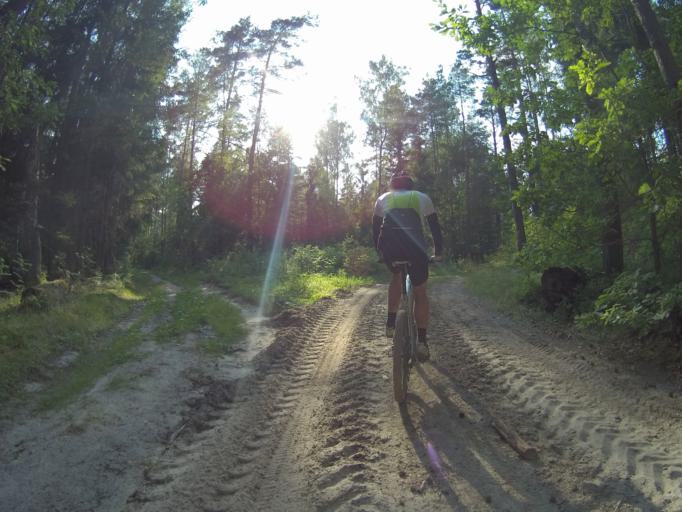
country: RU
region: Vladimir
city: Orgtrud
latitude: 56.1180
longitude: 40.6299
